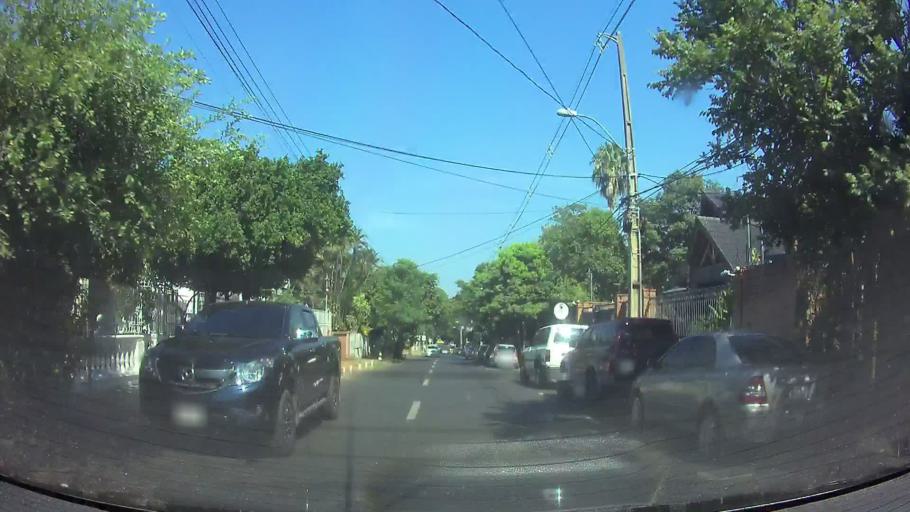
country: PY
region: Asuncion
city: Asuncion
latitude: -25.2894
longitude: -57.5700
